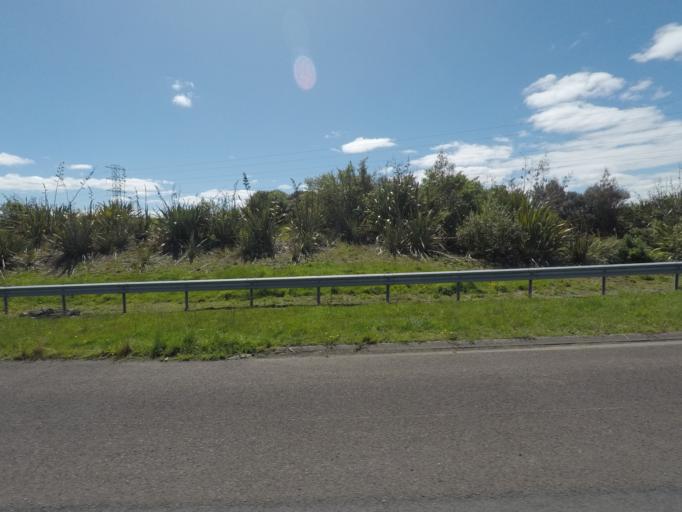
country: NZ
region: Auckland
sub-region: Auckland
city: Rosebank
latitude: -36.8045
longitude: 174.6050
